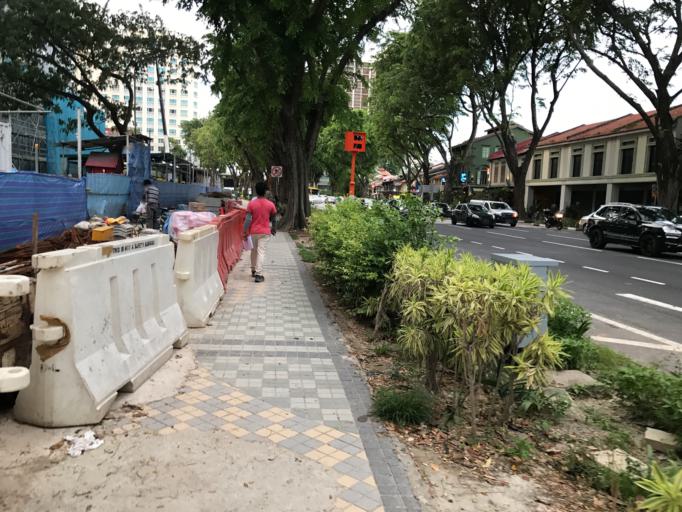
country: SG
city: Singapore
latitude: 1.2999
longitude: 103.8593
